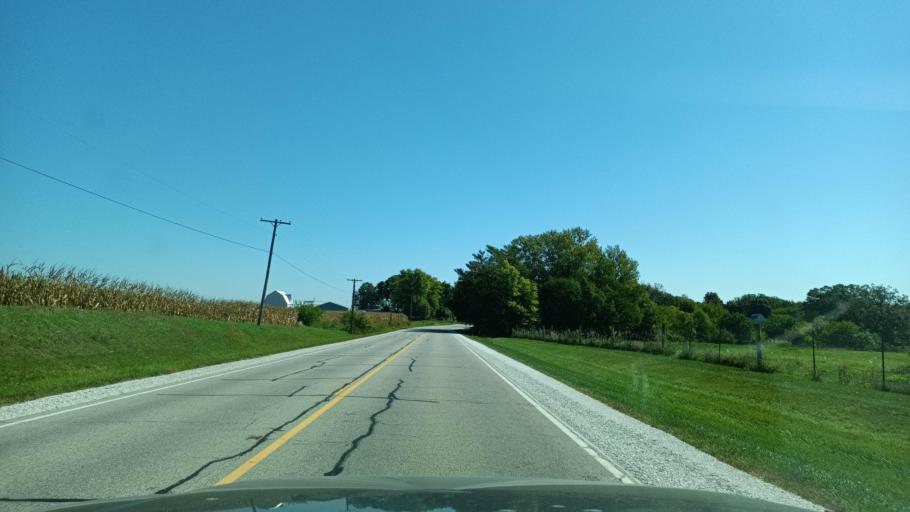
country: US
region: Illinois
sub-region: Peoria County
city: Hanna City
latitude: 40.7945
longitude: -89.7795
